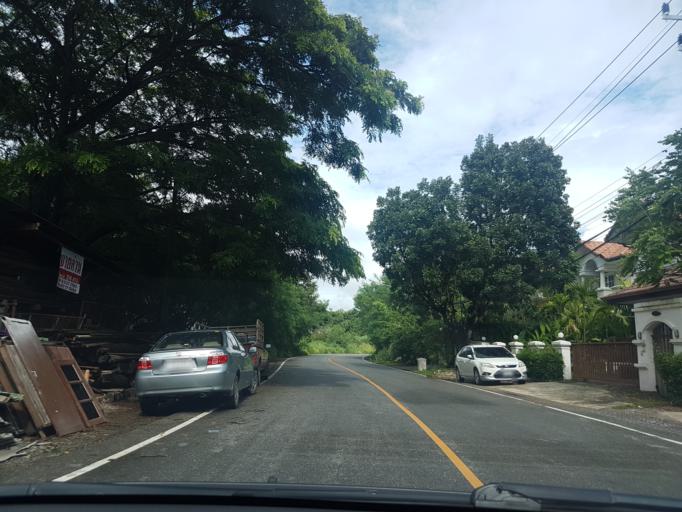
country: TH
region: Chiang Mai
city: San Sai
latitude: 18.8361
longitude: 99.0086
